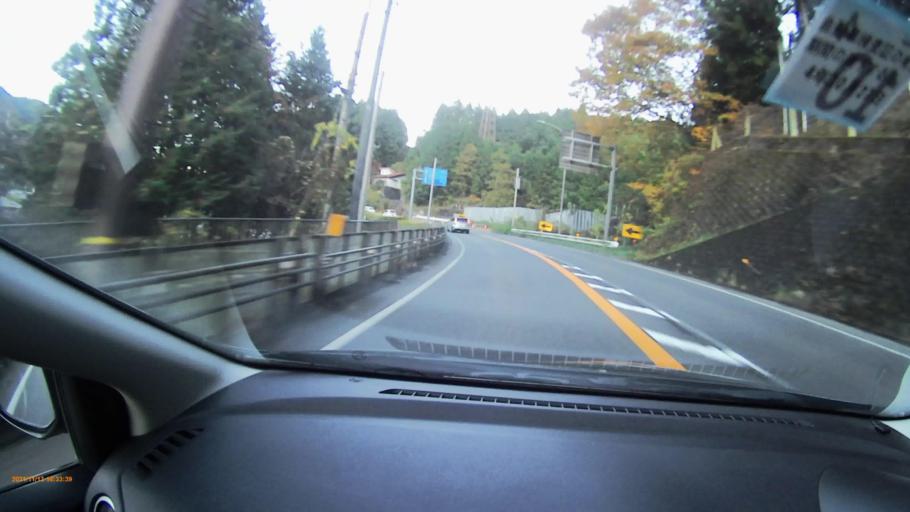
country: JP
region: Gifu
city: Nakatsugawa
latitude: 35.5864
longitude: 137.5968
